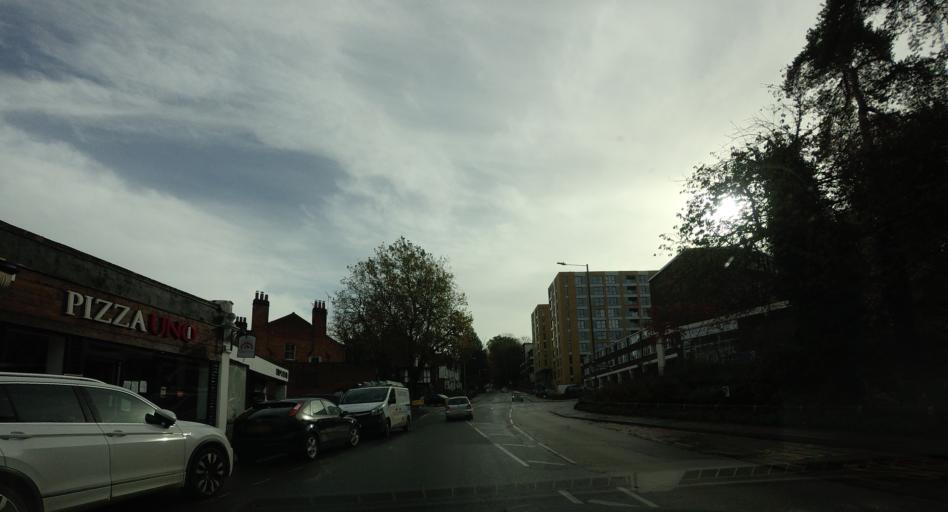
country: GB
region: England
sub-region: Kent
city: Sevenoaks
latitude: 51.2768
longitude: 0.1835
